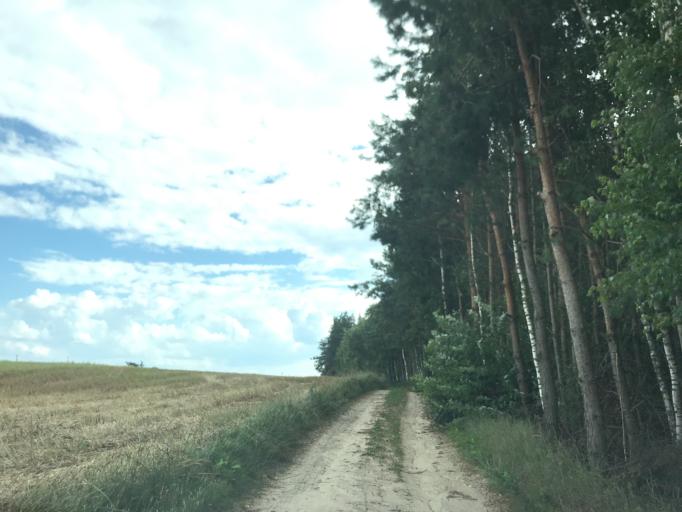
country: PL
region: Kujawsko-Pomorskie
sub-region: Powiat brodnicki
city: Brzozie
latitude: 53.3217
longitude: 19.6884
